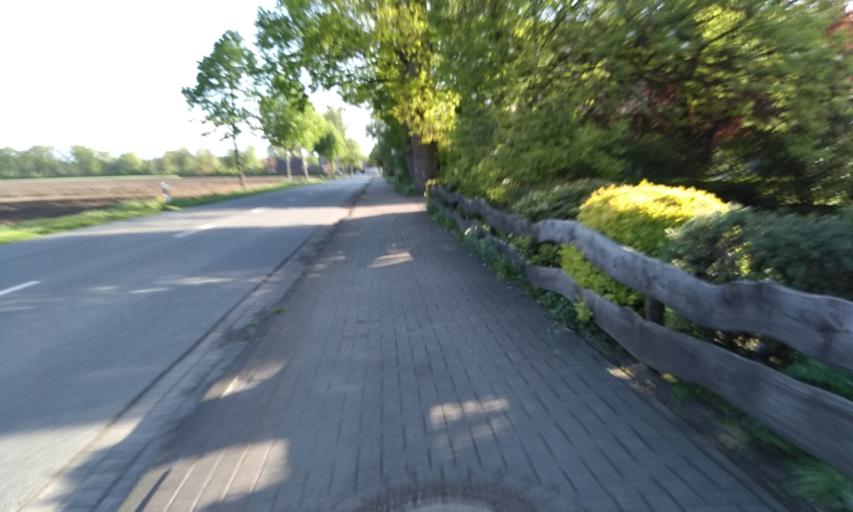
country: DE
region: Lower Saxony
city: Sauensiek
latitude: 53.4103
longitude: 9.5477
